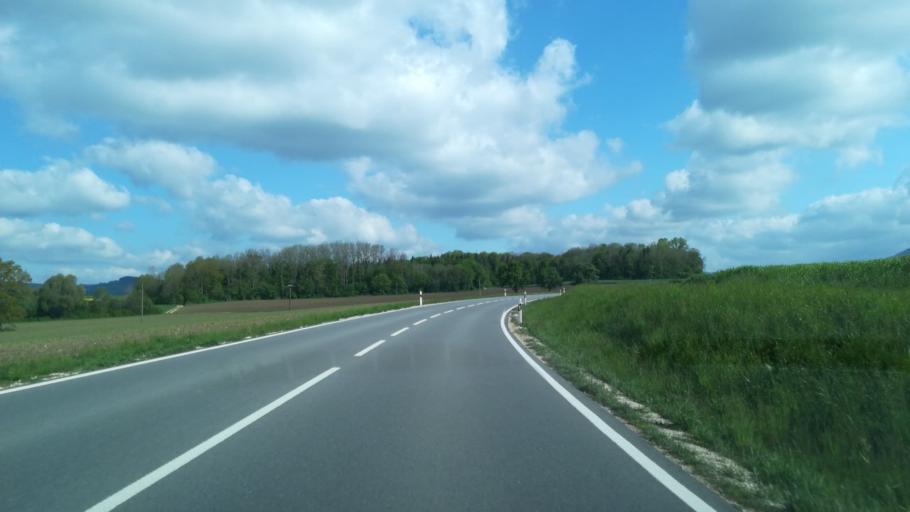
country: CH
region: Schaffhausen
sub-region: Bezirk Reiat
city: Thayngen
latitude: 47.7829
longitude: 8.7149
